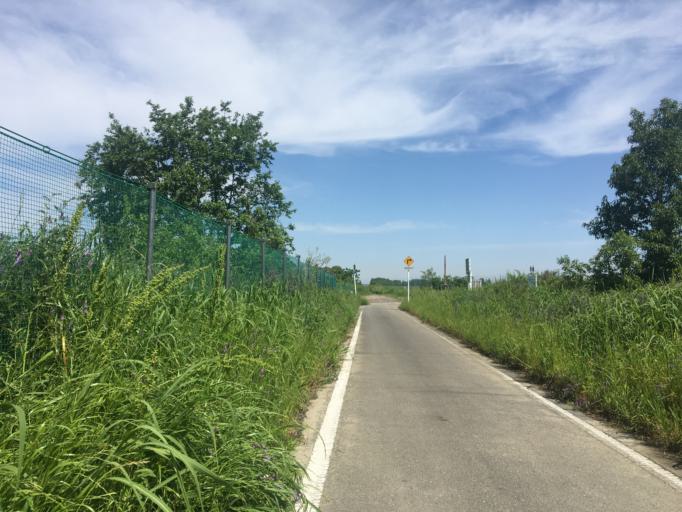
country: JP
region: Saitama
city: Shiki
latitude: 35.8750
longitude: 139.5774
